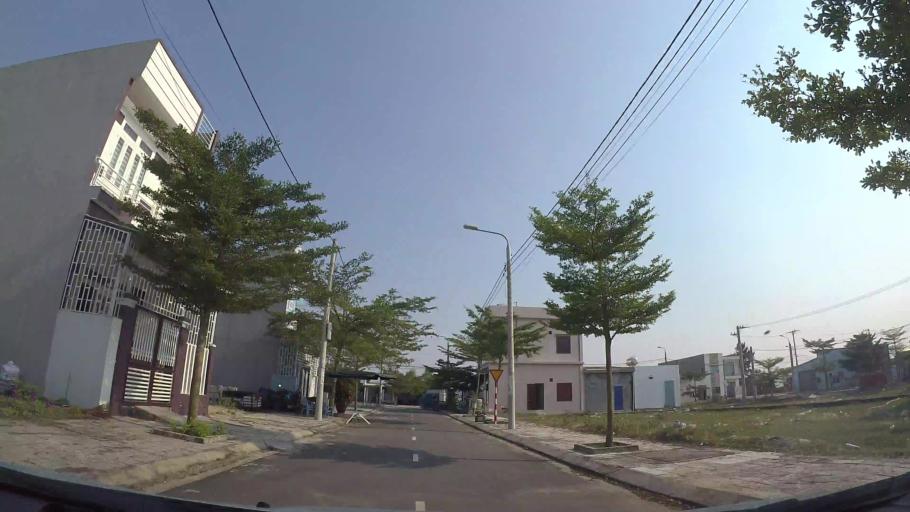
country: VN
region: Quang Nam
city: Quang Nam
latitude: 15.9487
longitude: 108.2625
